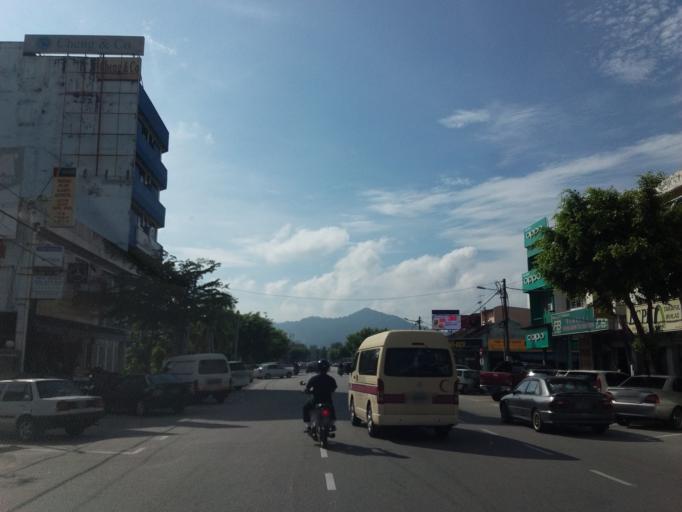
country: MY
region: Johor
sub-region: Daerah Batu Pahat
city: Batu Pahat
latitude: 1.8504
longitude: 102.9312
